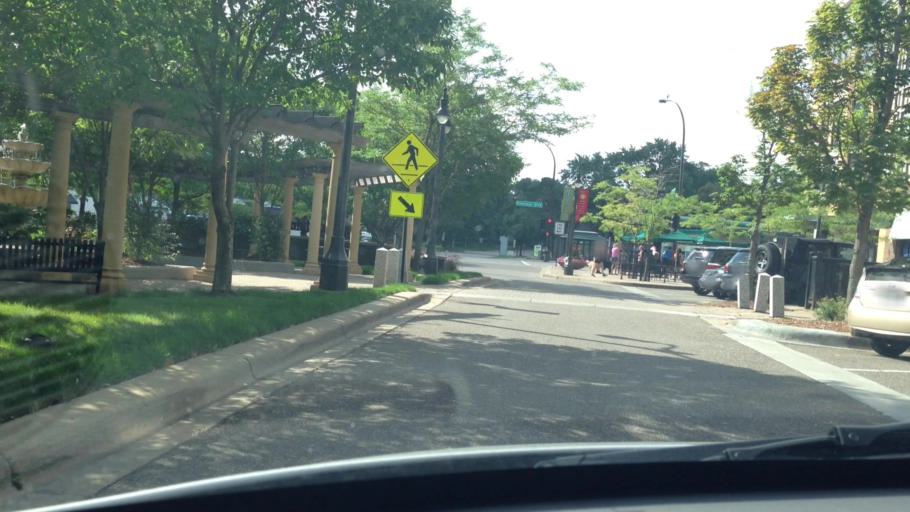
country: US
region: Minnesota
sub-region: Hennepin County
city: Saint Louis Park
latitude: 44.9340
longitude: -93.3404
